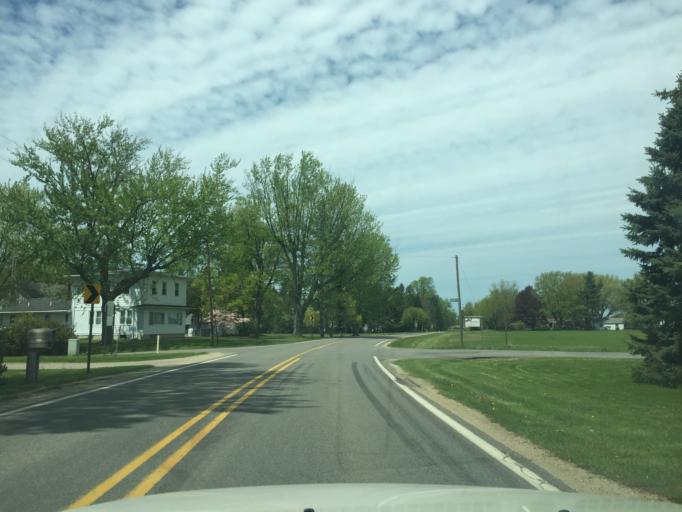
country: US
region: Michigan
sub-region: Berrien County
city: Stevensville
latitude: 41.9788
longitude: -86.4967
